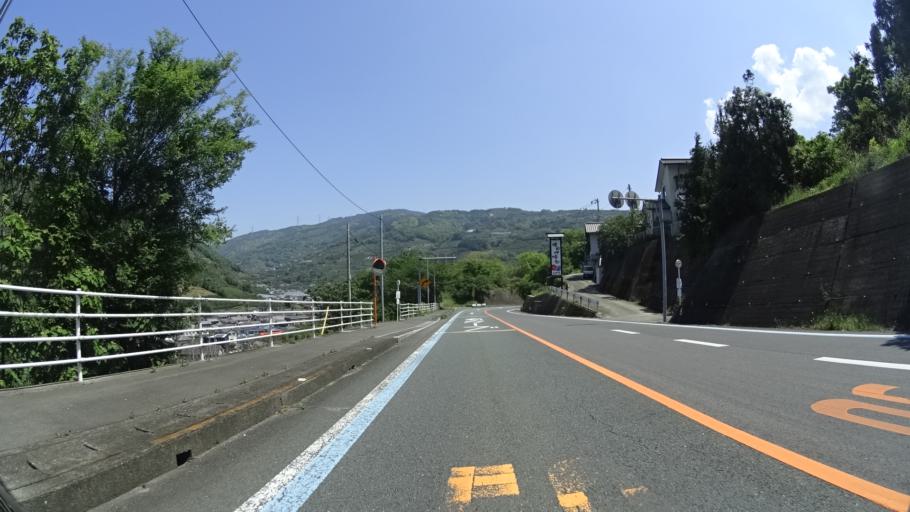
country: JP
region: Ehime
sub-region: Nishiuwa-gun
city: Ikata-cho
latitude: 33.4898
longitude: 132.3926
